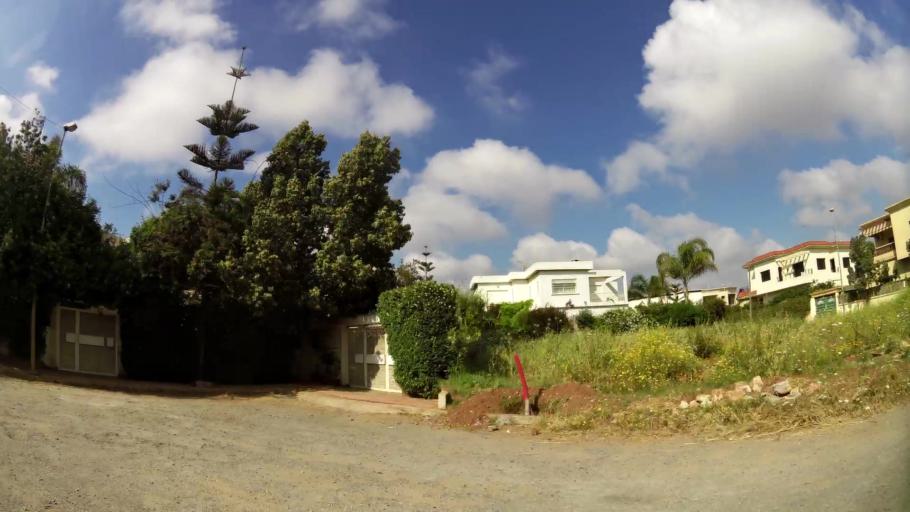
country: MA
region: Rabat-Sale-Zemmour-Zaer
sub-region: Skhirate-Temara
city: Temara
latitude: 33.9512
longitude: -6.8818
